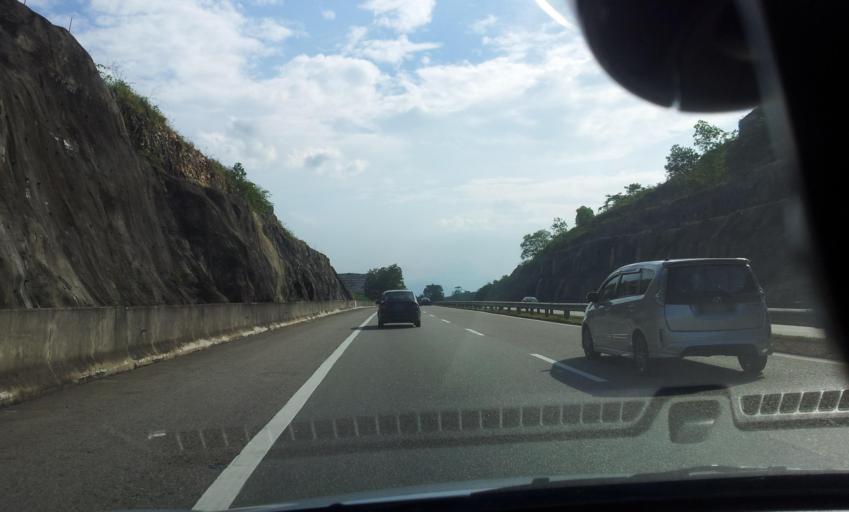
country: MY
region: Pahang
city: Mentekab
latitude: 3.5131
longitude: 102.1355
